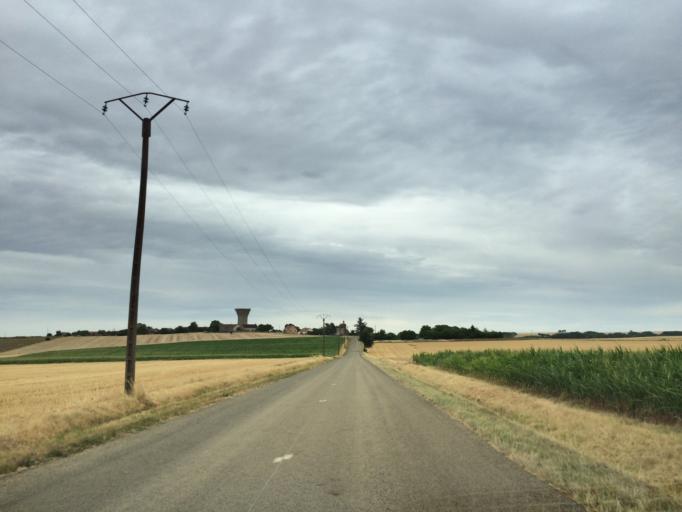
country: FR
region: Bourgogne
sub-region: Departement de l'Yonne
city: Aillant-sur-Tholon
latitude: 47.8712
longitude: 3.3302
